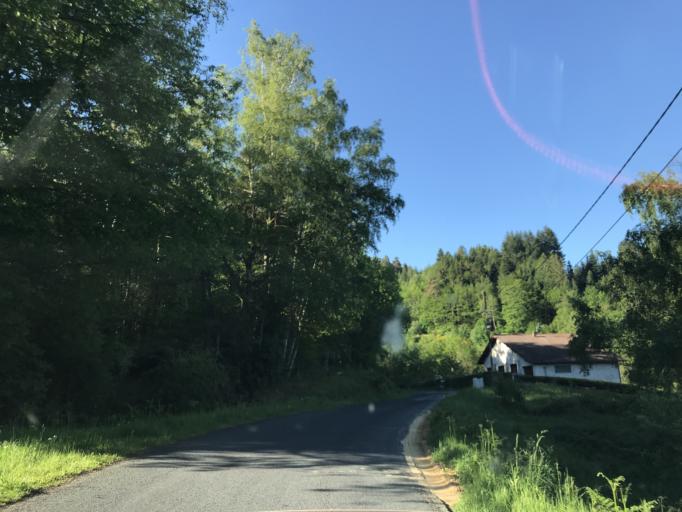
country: FR
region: Auvergne
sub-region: Departement du Puy-de-Dome
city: Job
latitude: 45.6987
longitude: 3.6930
